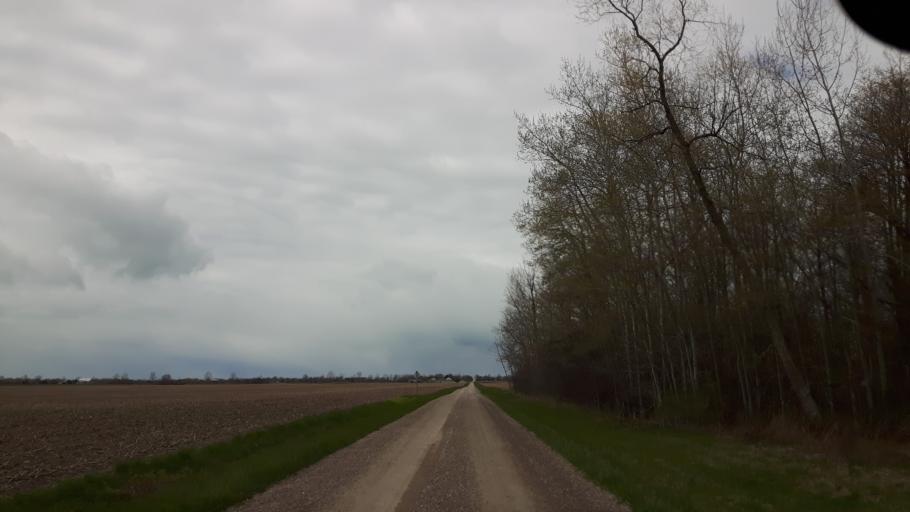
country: CA
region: Ontario
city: Bluewater
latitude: 43.4721
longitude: -81.6815
